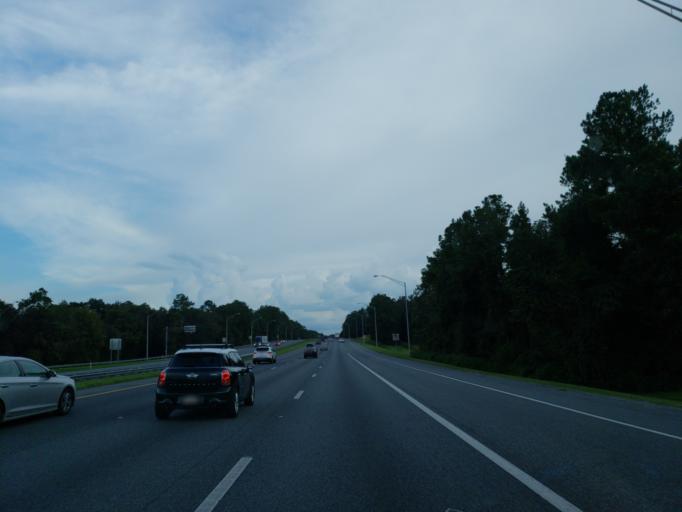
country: US
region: Florida
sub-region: Alachua County
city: High Springs
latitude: 29.9966
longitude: -82.5925
